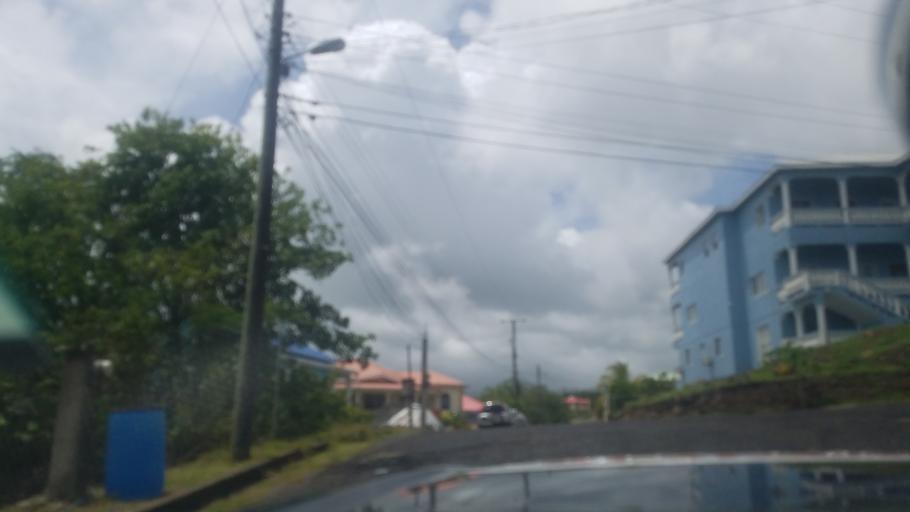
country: LC
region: Laborie Quarter
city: Laborie
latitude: 13.7481
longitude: -60.9767
